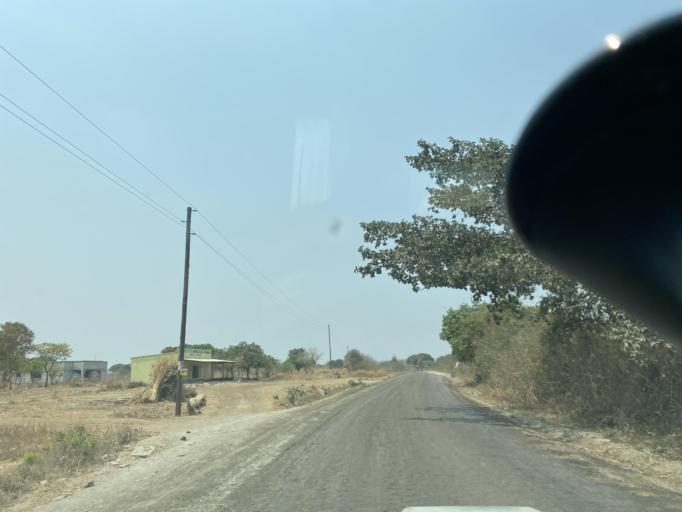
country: ZM
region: Lusaka
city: Lusaka
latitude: -15.5608
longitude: 28.4335
